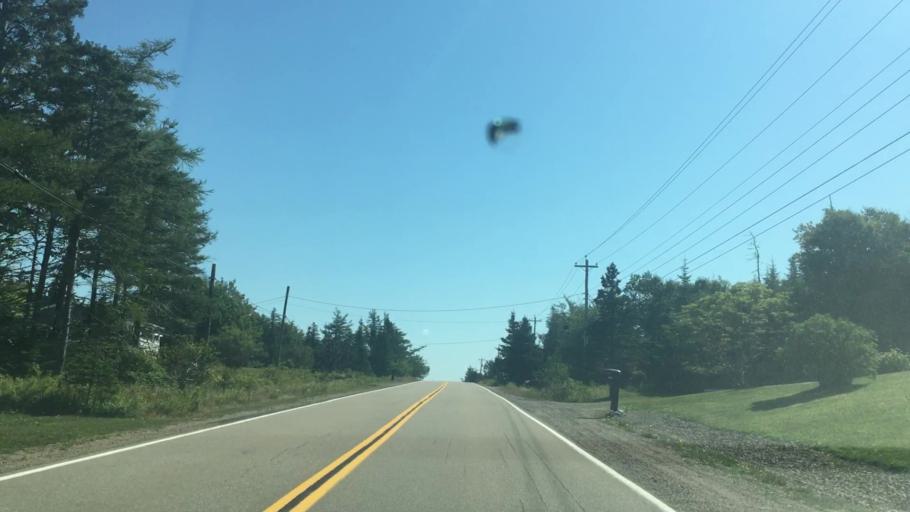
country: CA
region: Nova Scotia
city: Antigonish
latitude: 45.0245
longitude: -62.0240
